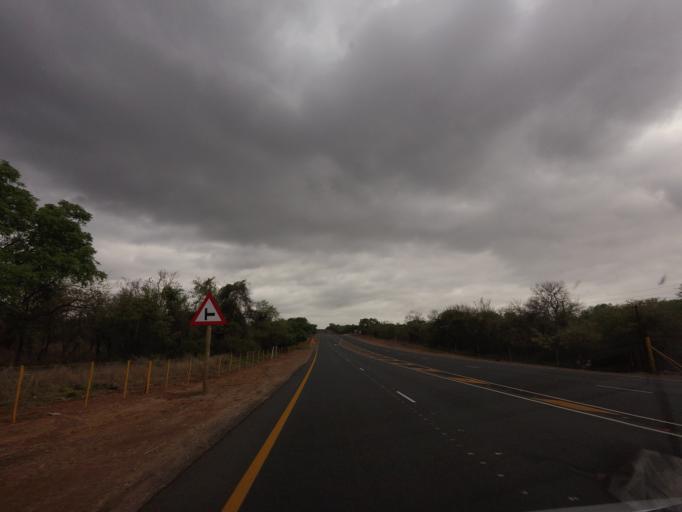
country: ZA
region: Mpumalanga
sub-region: Ehlanzeni District
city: Komatipoort
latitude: -25.4402
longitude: 31.7640
